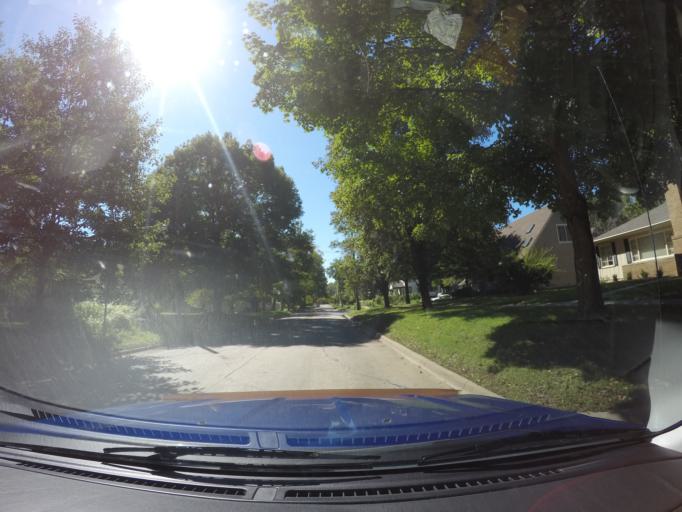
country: US
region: Kansas
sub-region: Douglas County
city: Lawrence
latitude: 38.9521
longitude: -95.2328
